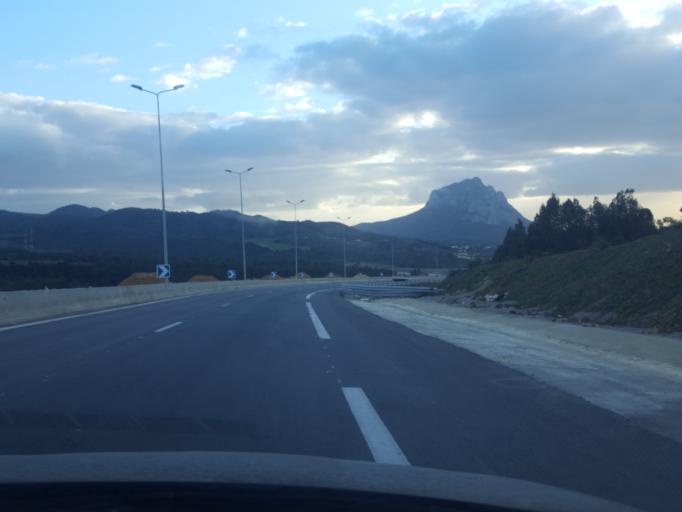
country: TN
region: Tunis
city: Hammam-Lif
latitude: 36.6542
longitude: 10.3720
